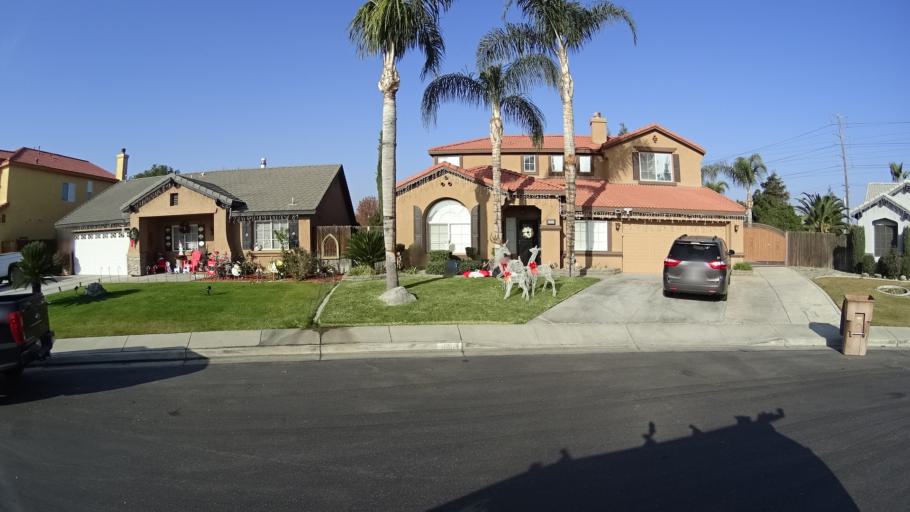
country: US
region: California
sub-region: Kern County
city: Greenacres
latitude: 35.4166
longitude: -119.0934
